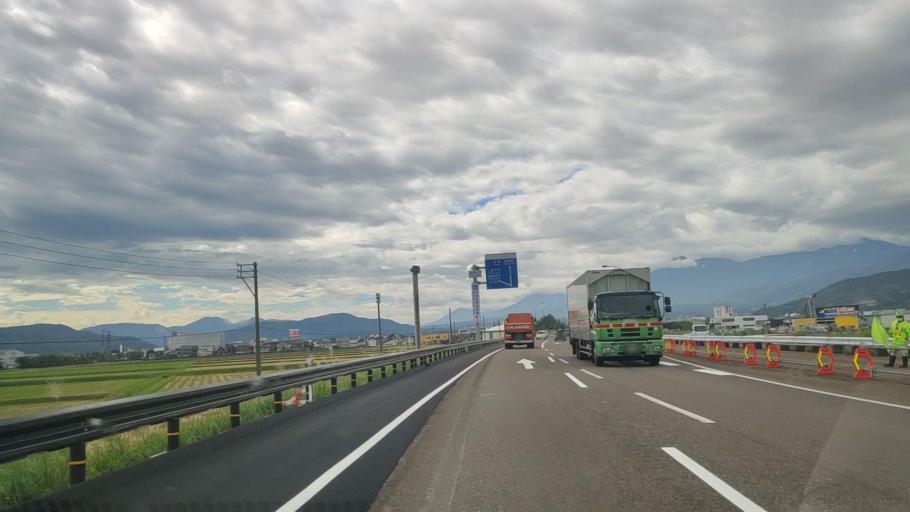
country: JP
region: Niigata
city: Arai
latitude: 37.0632
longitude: 138.2624
